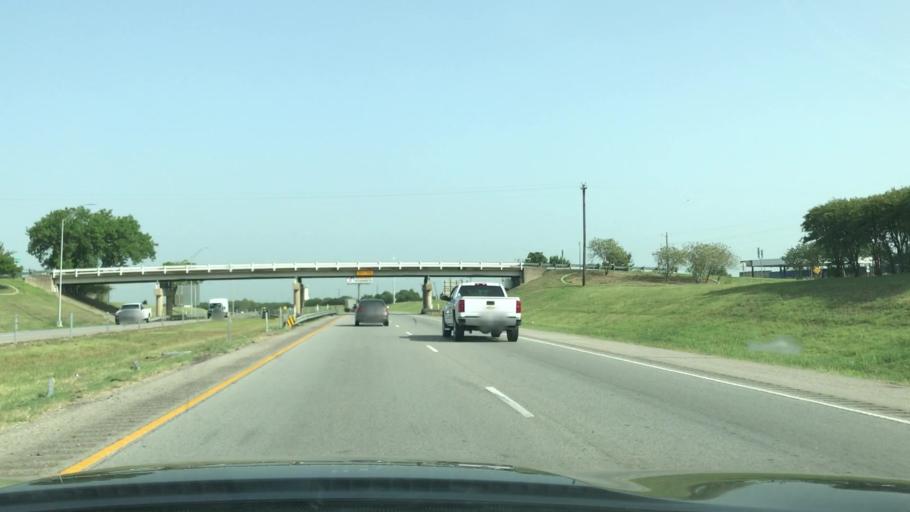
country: US
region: Texas
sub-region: Kaufman County
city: Forney
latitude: 32.7689
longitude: -96.4877
